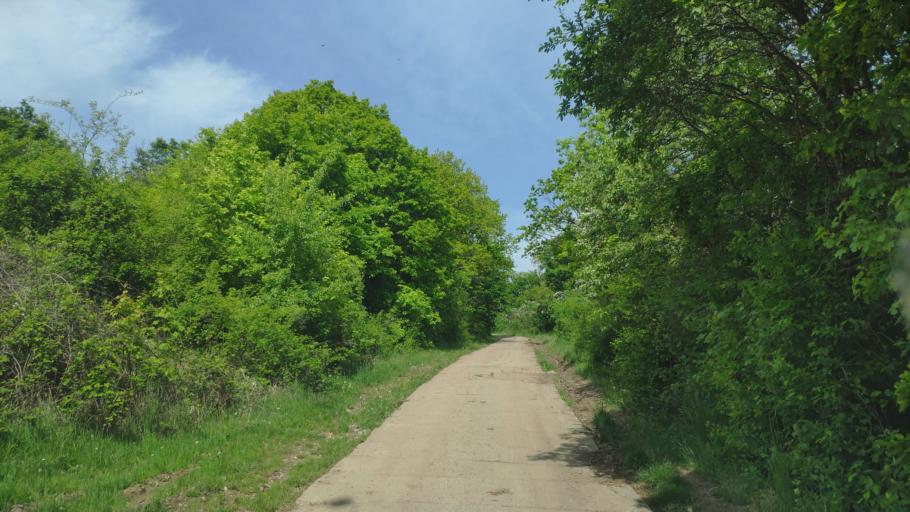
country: SK
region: Kosicky
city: Secovce
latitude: 48.6882
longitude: 21.6047
